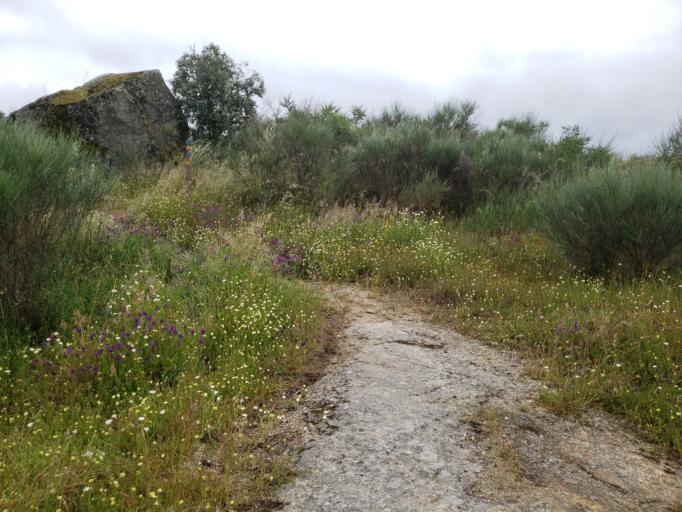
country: ES
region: Extremadura
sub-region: Provincia de Caceres
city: Malpartida de Caceres
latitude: 39.4209
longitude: -6.5046
